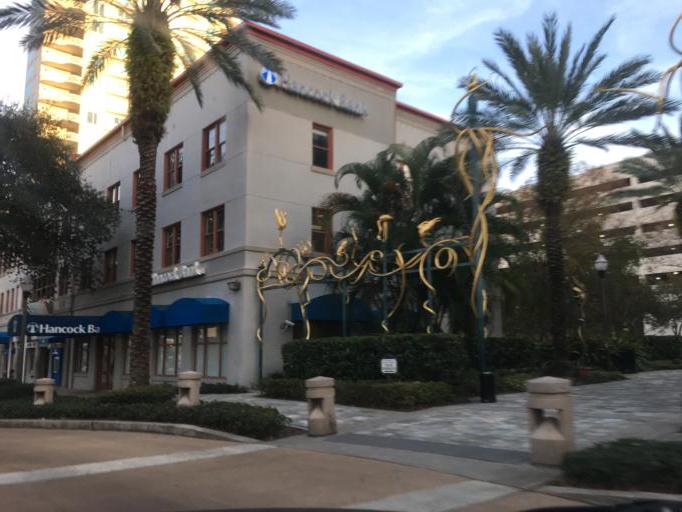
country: US
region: Florida
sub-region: Pinellas County
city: Saint Petersburg
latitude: 27.7735
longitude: -82.6347
